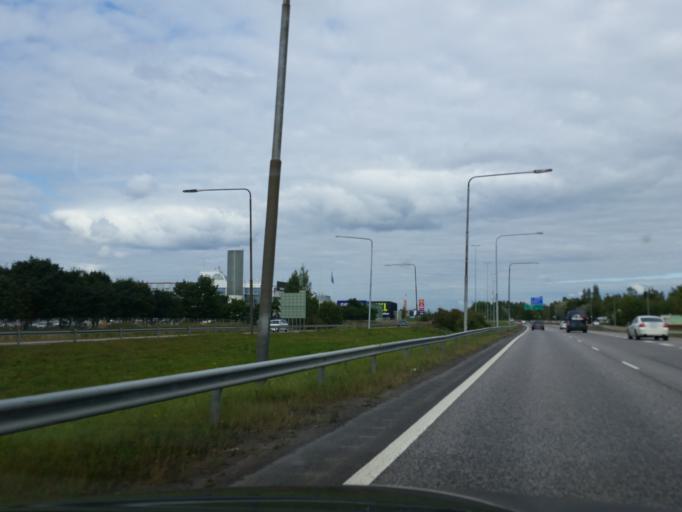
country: FI
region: Uusimaa
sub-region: Helsinki
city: Vantaa
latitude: 60.2730
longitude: 24.9753
